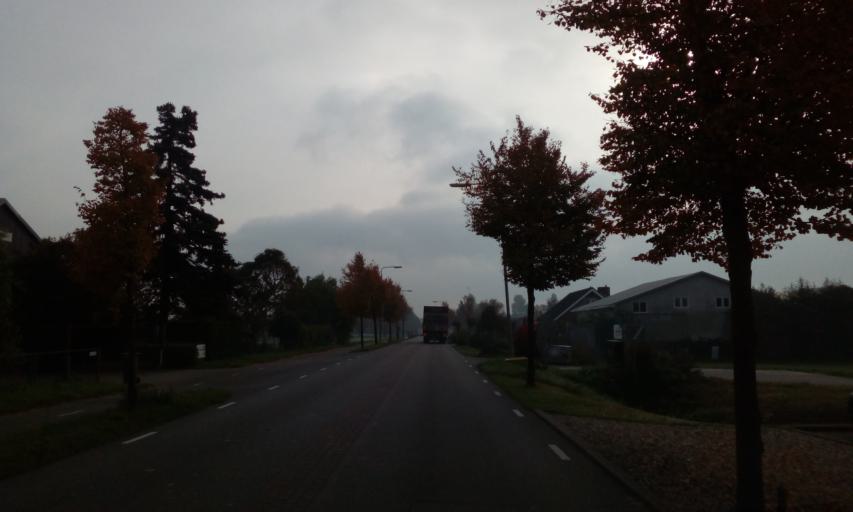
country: NL
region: South Holland
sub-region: Gemeente Waddinxveen
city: Groenswaard
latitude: 52.0344
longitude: 4.5920
